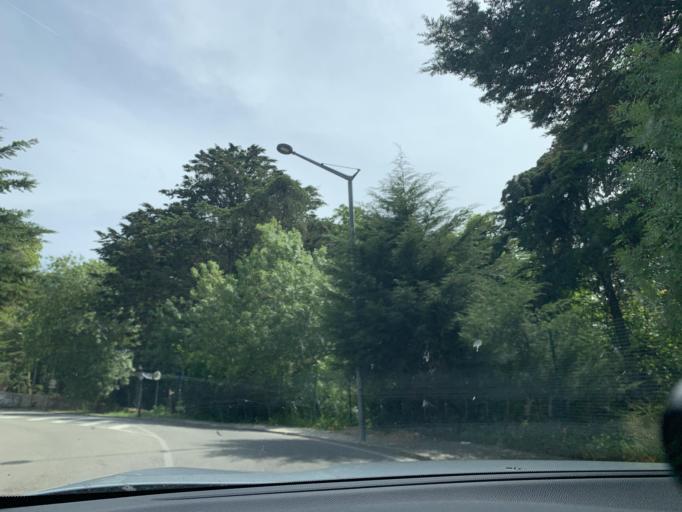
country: PT
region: Lisbon
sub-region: Sintra
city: Sintra
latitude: 38.8035
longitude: -9.3890
